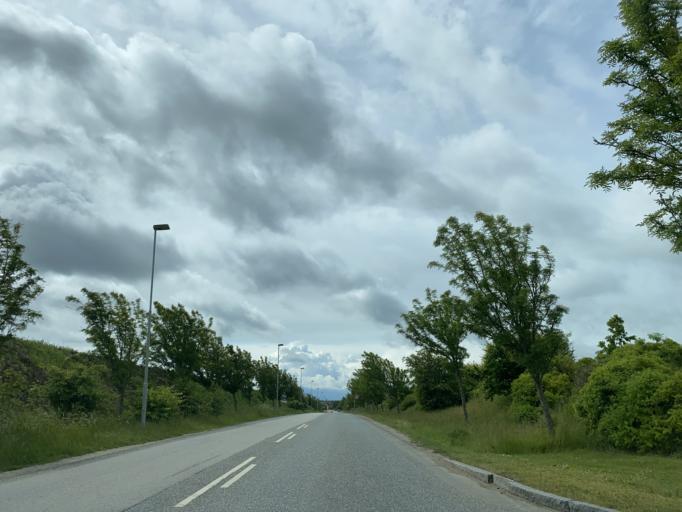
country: DK
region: Central Jutland
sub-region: Arhus Kommune
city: Stavtrup
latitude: 56.1910
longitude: 10.1308
